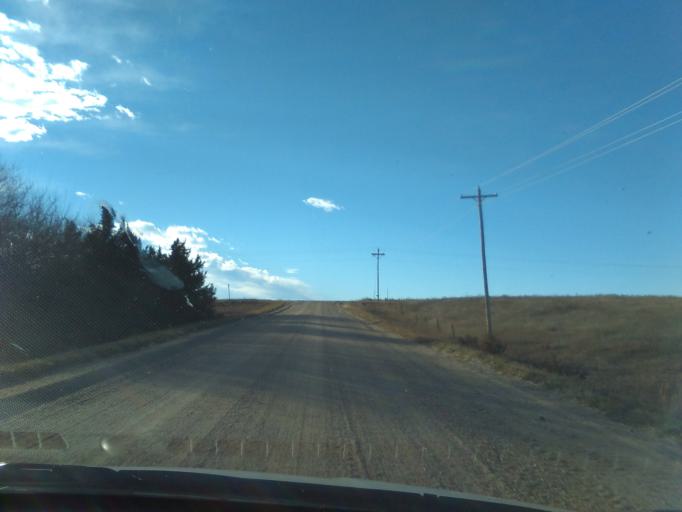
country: US
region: Nebraska
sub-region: Kearney County
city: Minden
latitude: 40.3649
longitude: -98.8931
